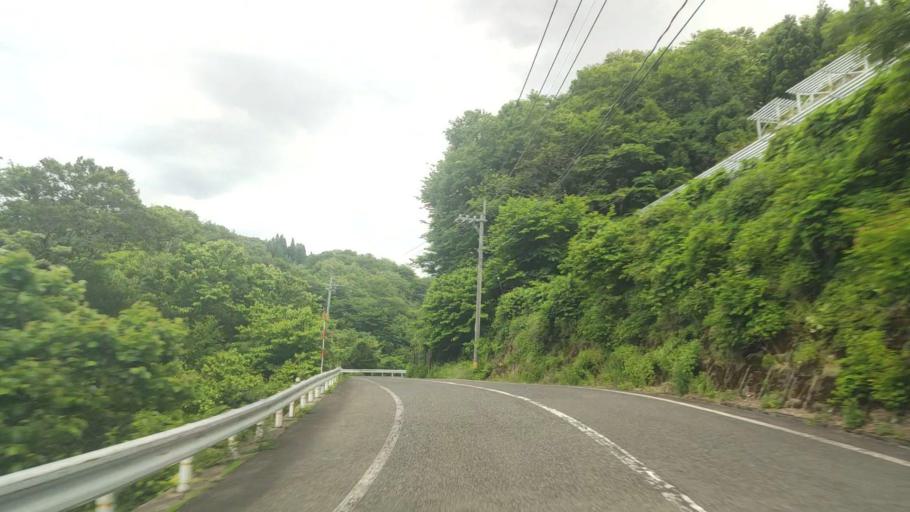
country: JP
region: Tottori
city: Kurayoshi
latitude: 35.3184
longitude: 134.0096
